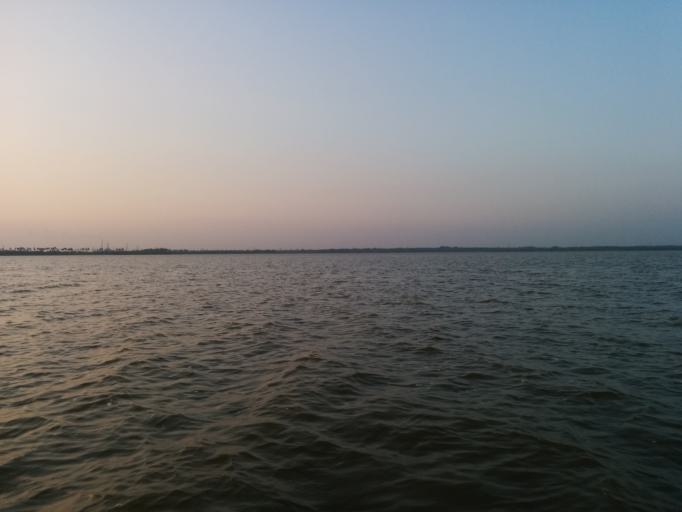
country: IN
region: Pondicherry
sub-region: Puducherry
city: Puducherry
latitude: 11.9484
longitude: 79.7479
